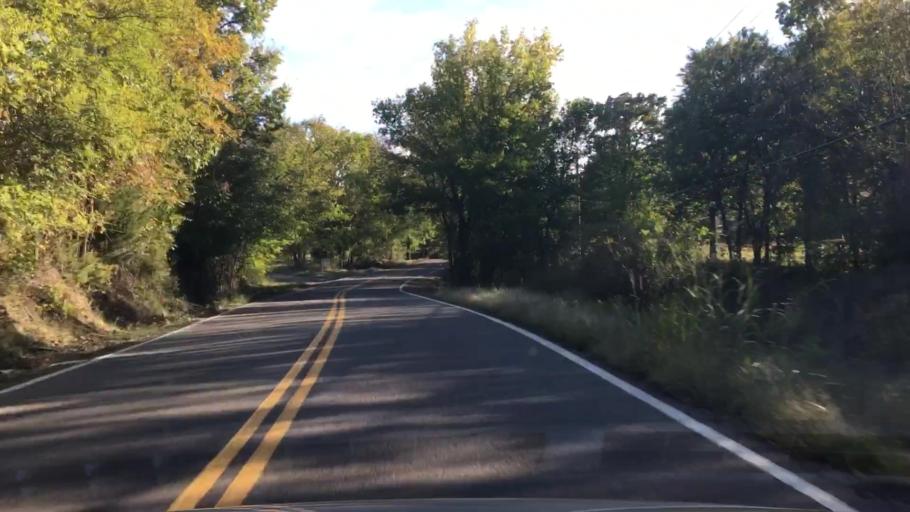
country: US
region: Oklahoma
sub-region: Muskogee County
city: Fort Gibson
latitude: 35.9252
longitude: -95.1541
